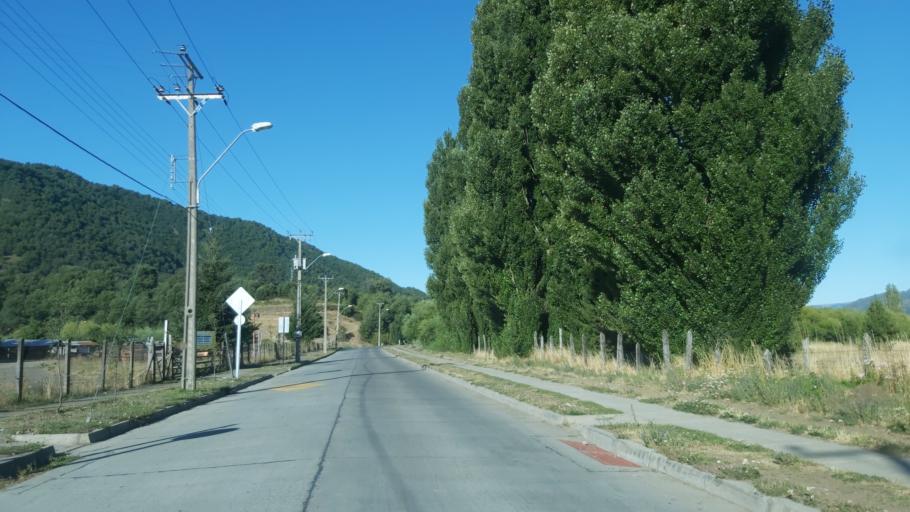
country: AR
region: Neuquen
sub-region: Departamento de Loncopue
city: Loncopue
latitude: -38.4489
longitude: -71.3679
